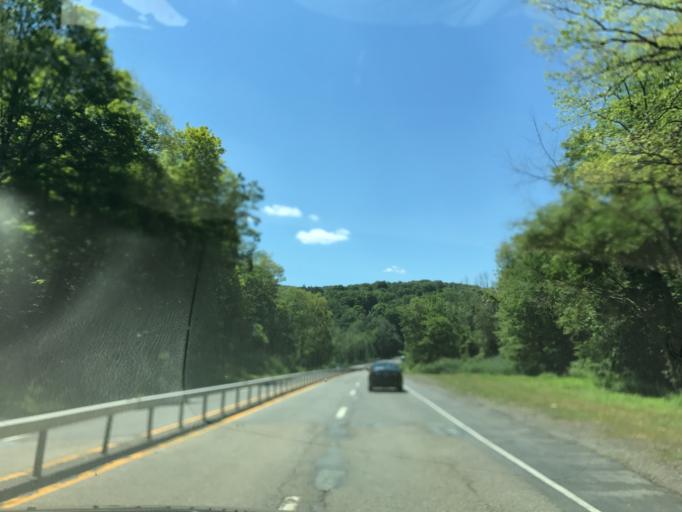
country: US
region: New York
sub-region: Dutchess County
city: Brinckerhoff
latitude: 41.5034
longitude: -73.7955
